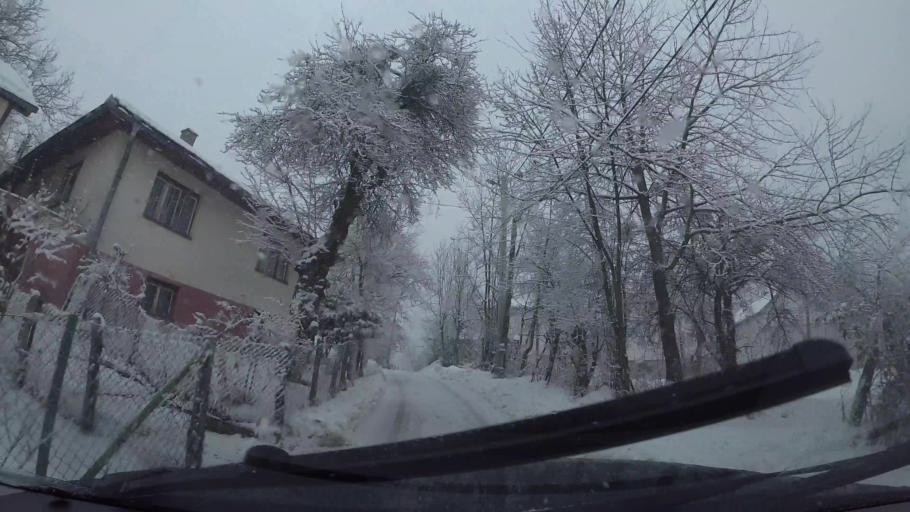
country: BA
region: Federation of Bosnia and Herzegovina
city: Kobilja Glava
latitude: 43.8504
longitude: 18.4552
